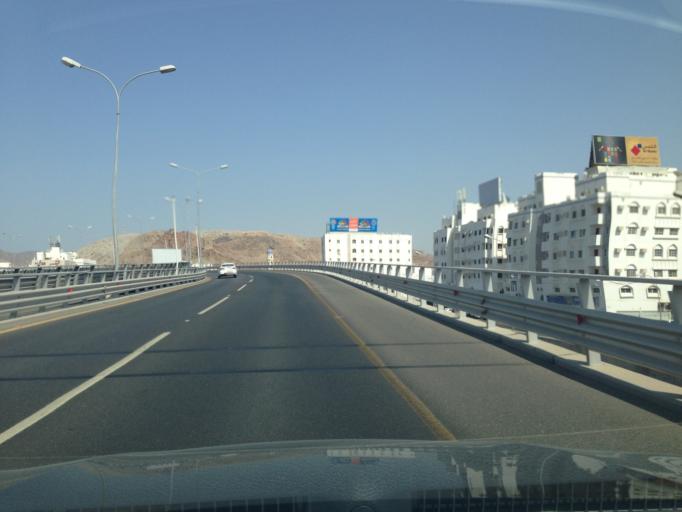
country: OM
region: Muhafazat Masqat
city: Muscat
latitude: 23.5865
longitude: 58.5370
